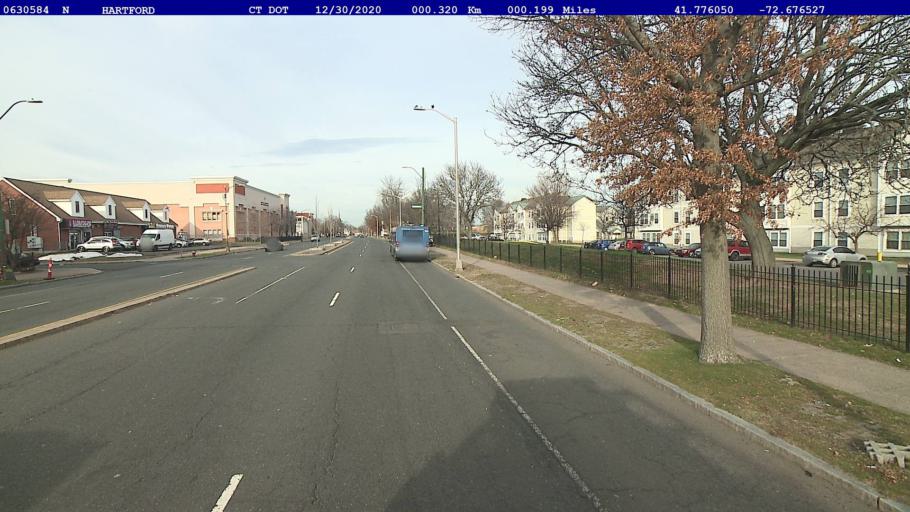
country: US
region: Connecticut
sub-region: Hartford County
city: Hartford
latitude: 41.7761
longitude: -72.6765
